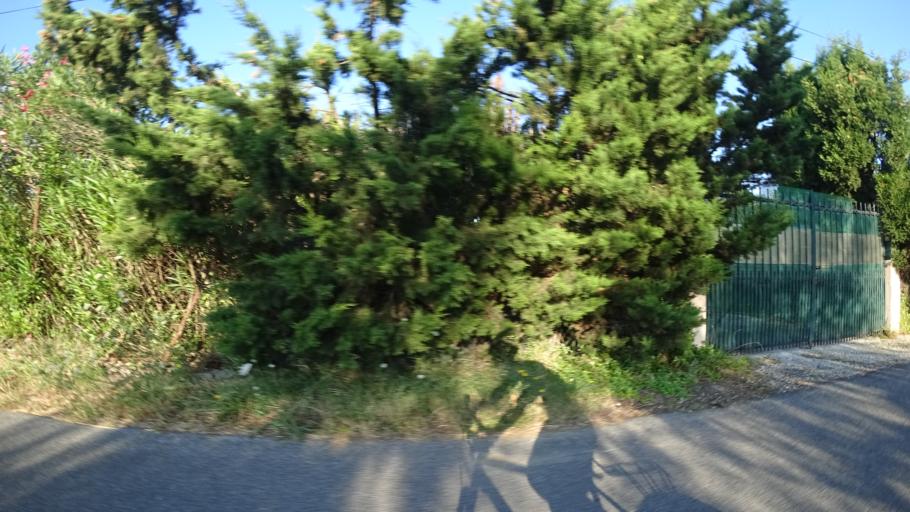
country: FR
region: Languedoc-Roussillon
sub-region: Departement des Pyrenees-Orientales
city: Sainte-Marie-Plage
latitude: 42.7275
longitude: 3.0287
